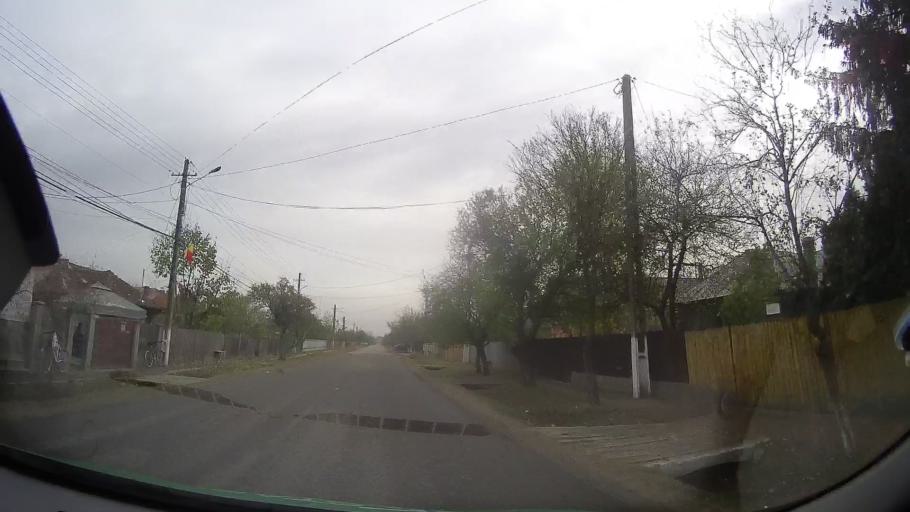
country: RO
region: Prahova
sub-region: Comuna Dumbrava
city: Dumbrava
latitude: 44.8696
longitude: 26.1953
